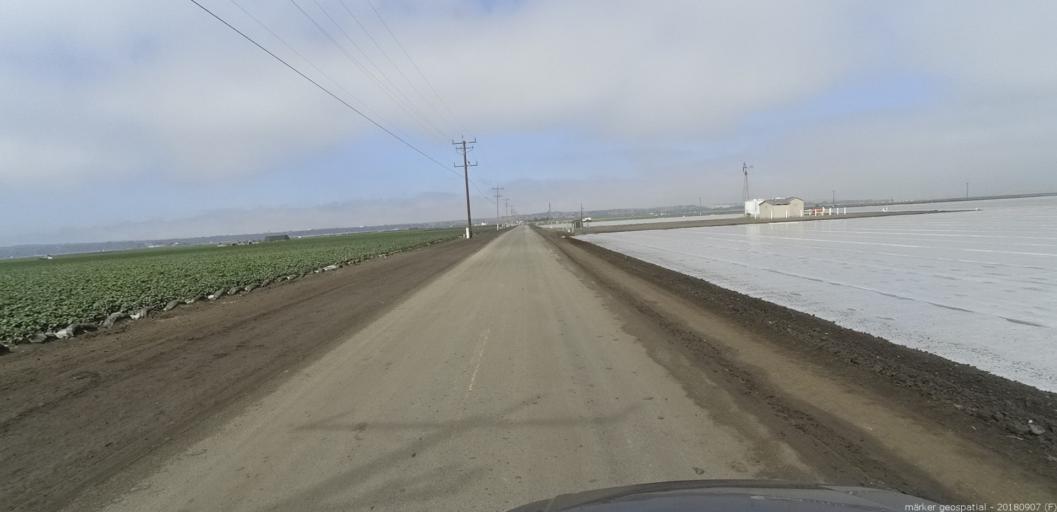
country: US
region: California
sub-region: Monterey County
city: Boronda
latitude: 36.6933
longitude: -121.7226
